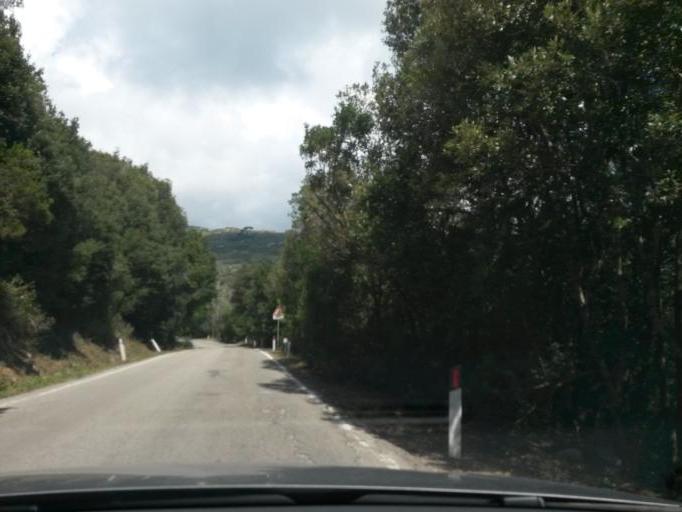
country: IT
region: Tuscany
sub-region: Provincia di Livorno
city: Campo nell'Elba
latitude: 42.7420
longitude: 10.2093
